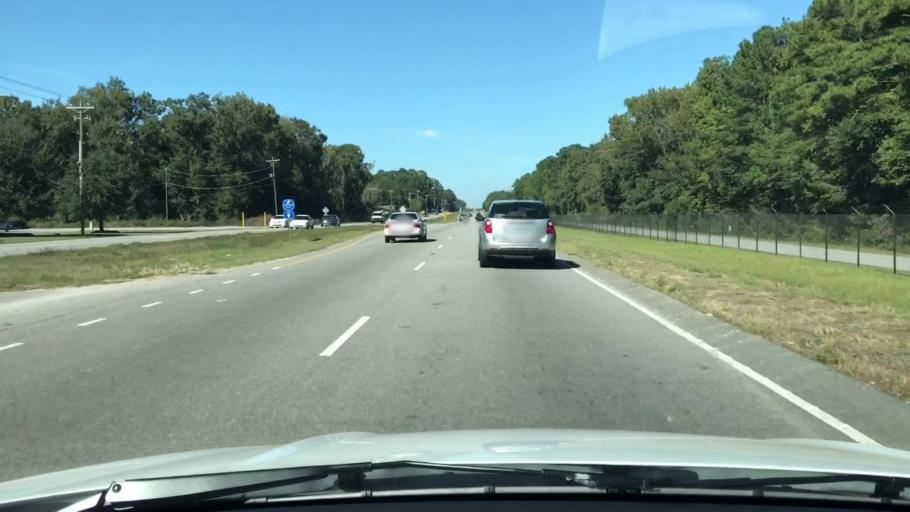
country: US
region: South Carolina
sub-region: Beaufort County
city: Burton
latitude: 32.4811
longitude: -80.7391
